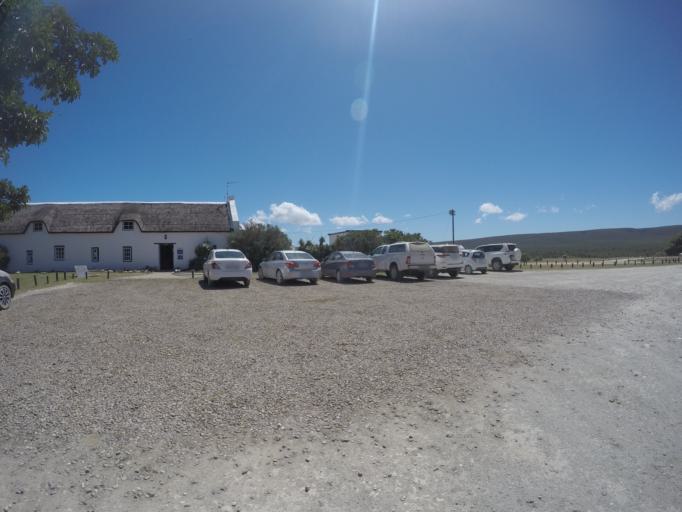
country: ZA
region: Western Cape
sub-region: Overberg District Municipality
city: Bredasdorp
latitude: -34.4542
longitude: 20.3997
